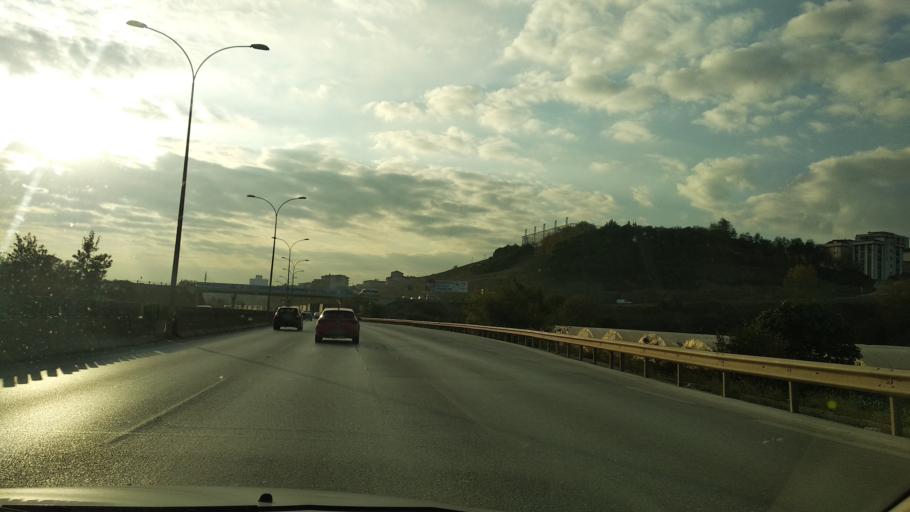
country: TR
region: Istanbul
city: Pendik
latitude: 40.8744
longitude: 29.2970
